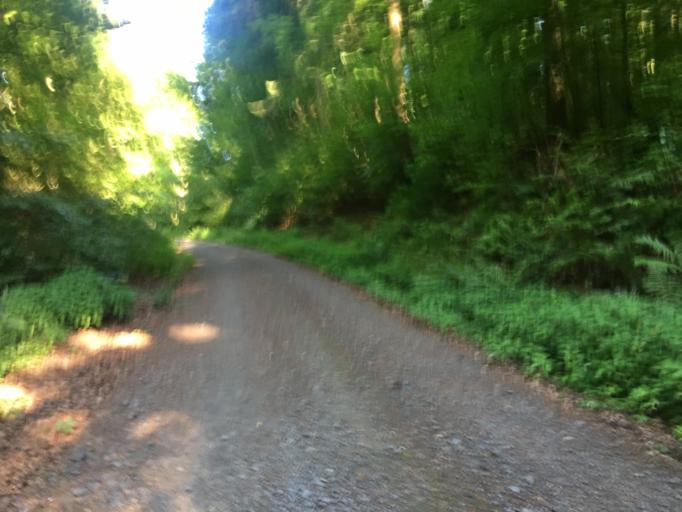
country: DE
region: Hesse
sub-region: Regierungsbezirk Darmstadt
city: Gelnhausen
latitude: 50.1749
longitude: 9.1629
